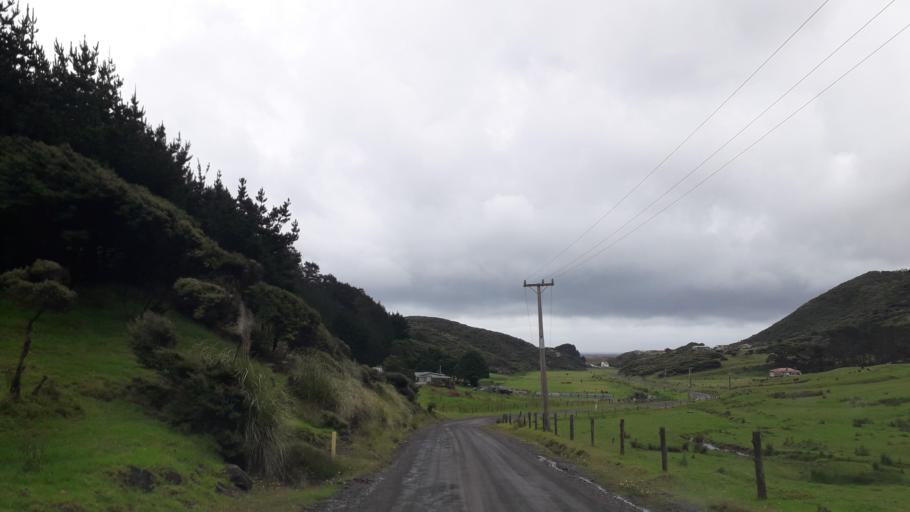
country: NZ
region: Northland
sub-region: Far North District
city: Ahipara
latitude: -35.4412
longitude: 173.2992
